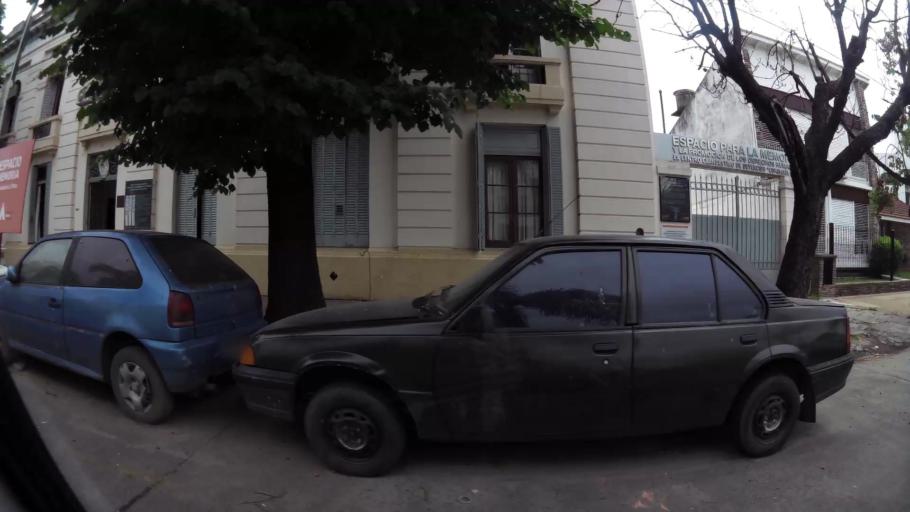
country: AR
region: Buenos Aires
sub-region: Partido de La Plata
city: La Plata
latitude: -34.9401
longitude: -57.9535
